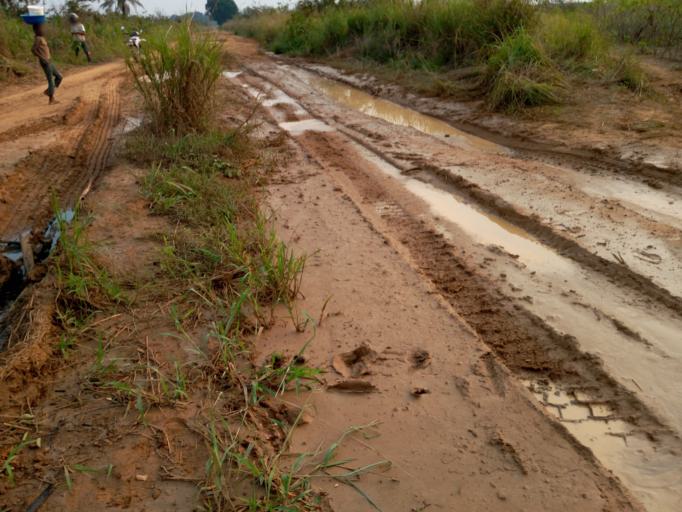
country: CD
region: Bandundu
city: Bandundu
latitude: -3.4284
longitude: 17.6073
